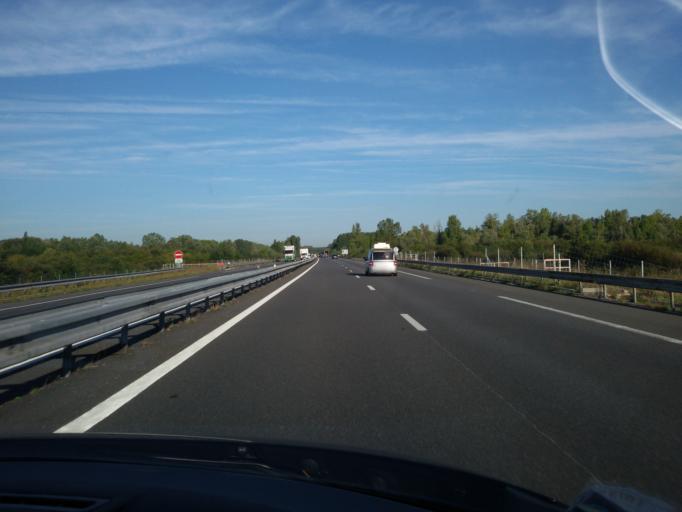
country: FR
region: Centre
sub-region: Departement du Cher
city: Vignoux-sur-Barangeon
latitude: 47.1961
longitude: 2.1507
